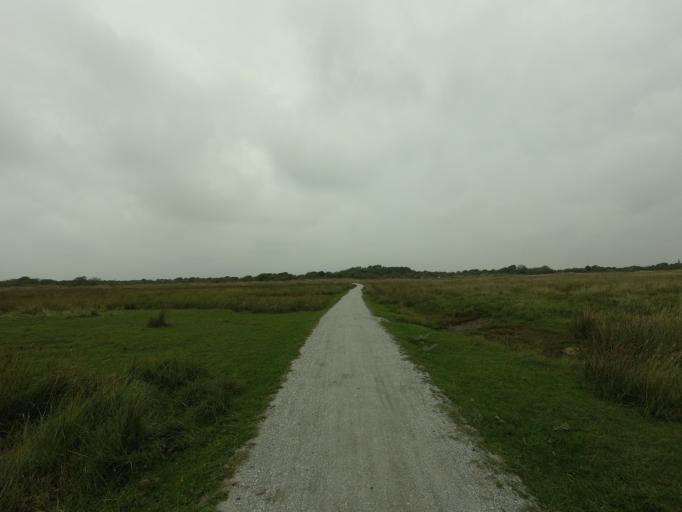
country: NL
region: Friesland
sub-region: Gemeente Schiermonnikoog
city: Schiermonnikoog
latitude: 53.4854
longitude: 6.2175
